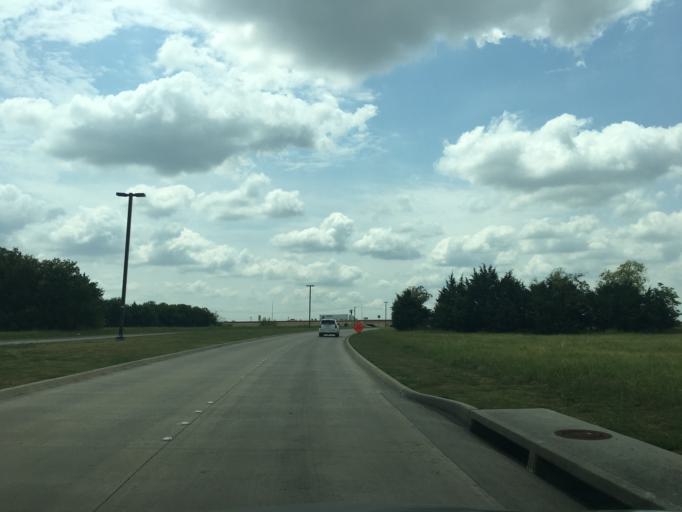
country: US
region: Texas
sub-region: Rockwall County
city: Rockwall
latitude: 32.9193
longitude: -96.4336
